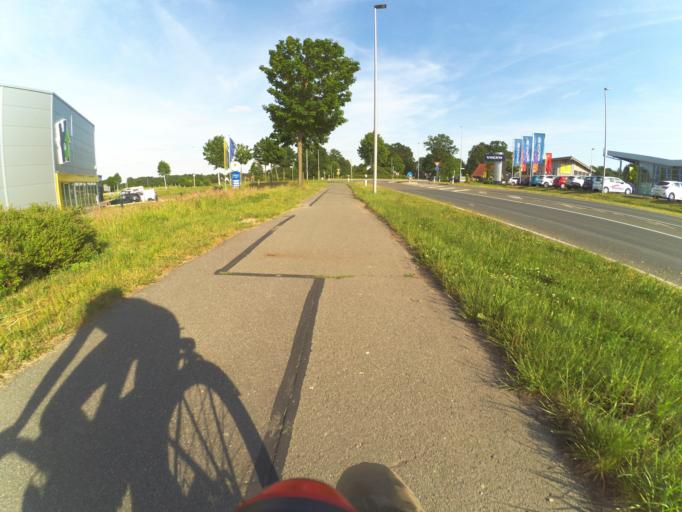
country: DE
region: North Rhine-Westphalia
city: Ibbenburen
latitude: 52.2599
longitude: 7.7261
